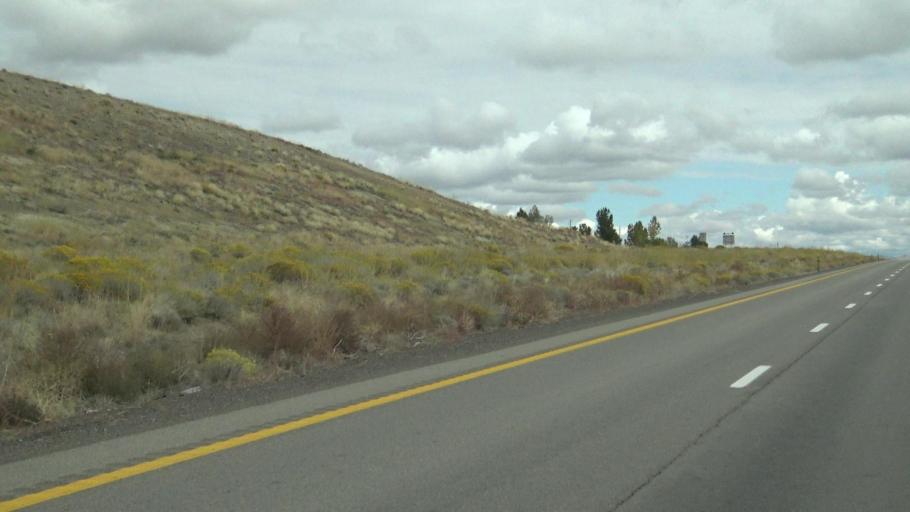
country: US
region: Nevada
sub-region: Elko County
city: Elko
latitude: 40.9270
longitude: -115.6756
